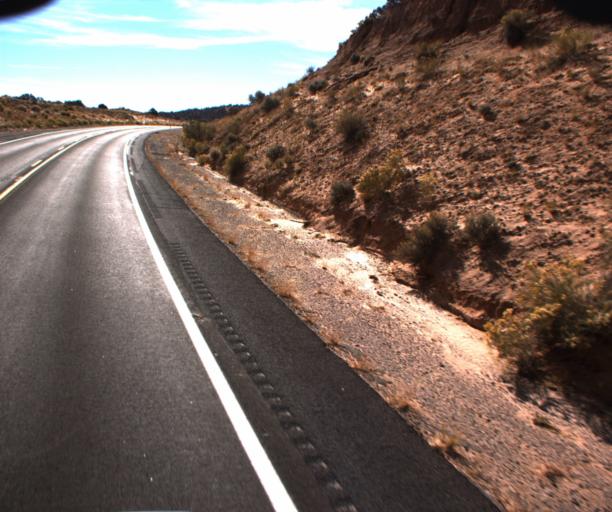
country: US
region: Arizona
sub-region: Coconino County
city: Kaibito
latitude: 36.6008
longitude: -110.9147
